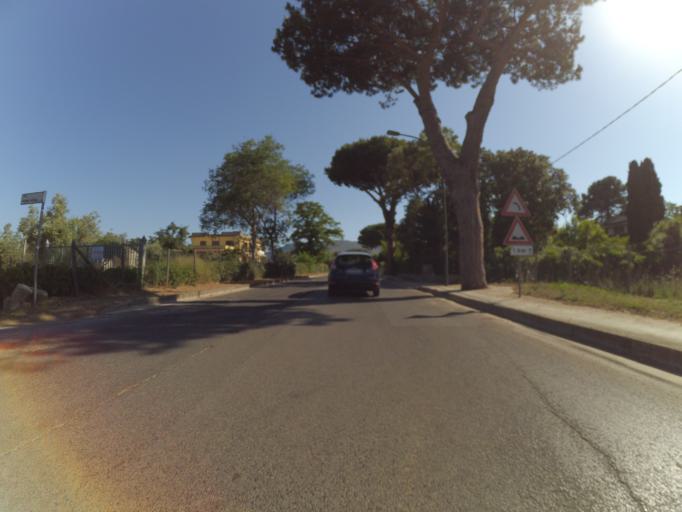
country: IT
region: Latium
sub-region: Provincia di Latina
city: San Felice Circeo
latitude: 41.2607
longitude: 13.0921
